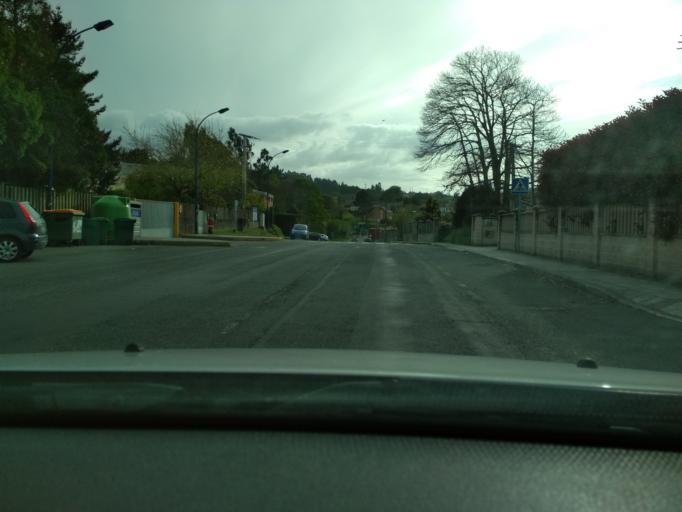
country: ES
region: Galicia
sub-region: Provincia da Coruna
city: Culleredo
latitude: 43.2897
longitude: -8.3766
